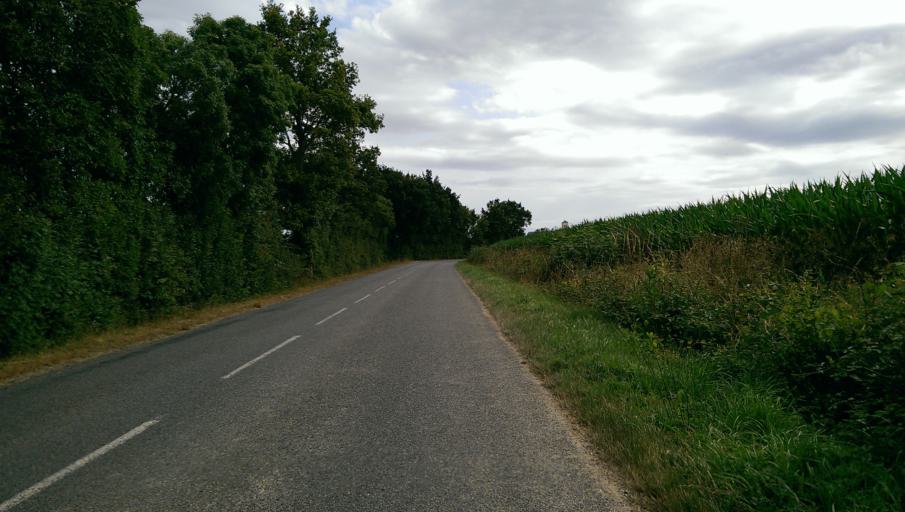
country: FR
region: Pays de la Loire
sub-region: Departement de la Loire-Atlantique
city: Vieillevigne
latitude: 46.9788
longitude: -1.4307
